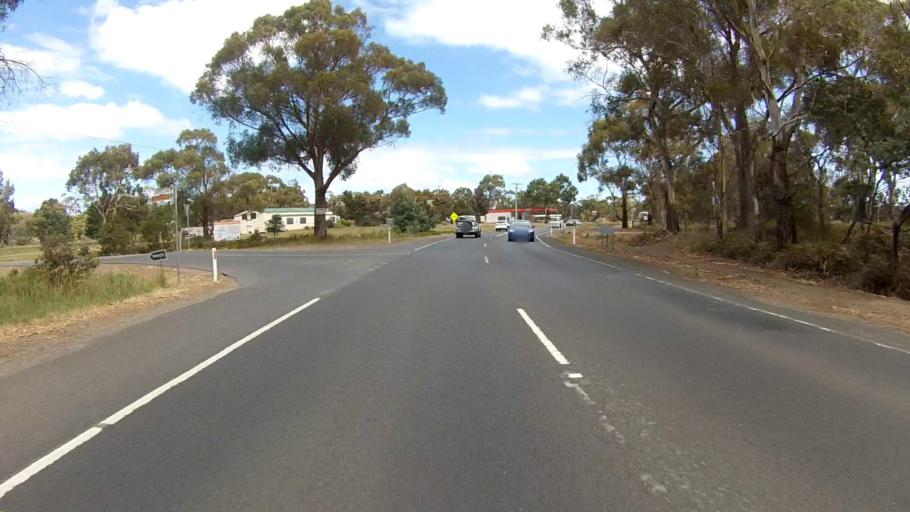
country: AU
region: Tasmania
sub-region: Sorell
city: Sorell
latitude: -42.8473
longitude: 147.6274
